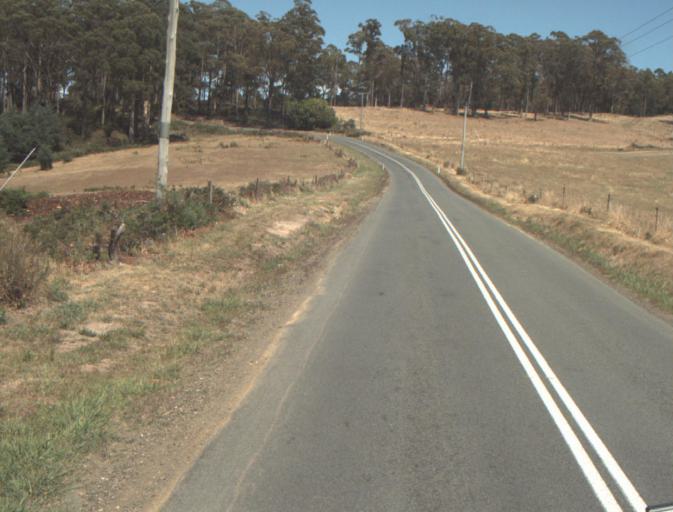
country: AU
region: Tasmania
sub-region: Launceston
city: Mayfield
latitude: -41.2728
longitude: 147.1277
